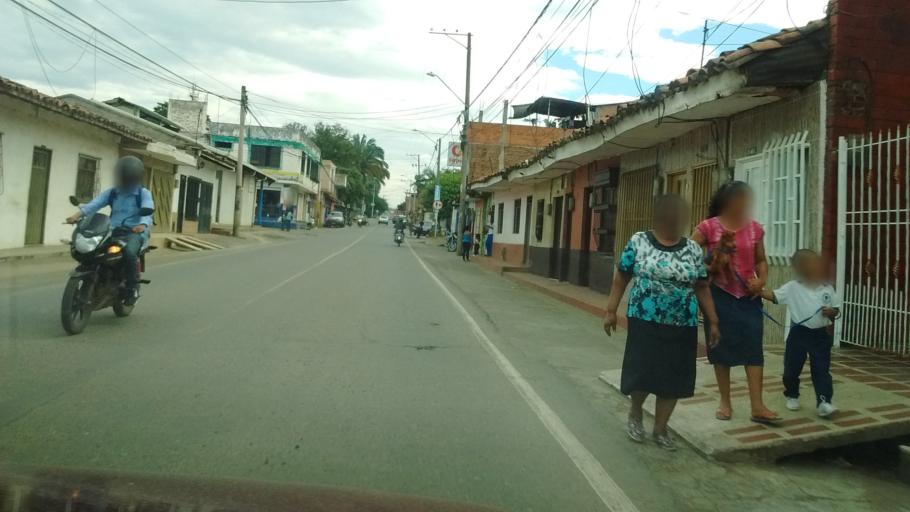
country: CO
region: Cauca
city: Santander de Quilichao
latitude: 3.0195
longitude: -76.4796
